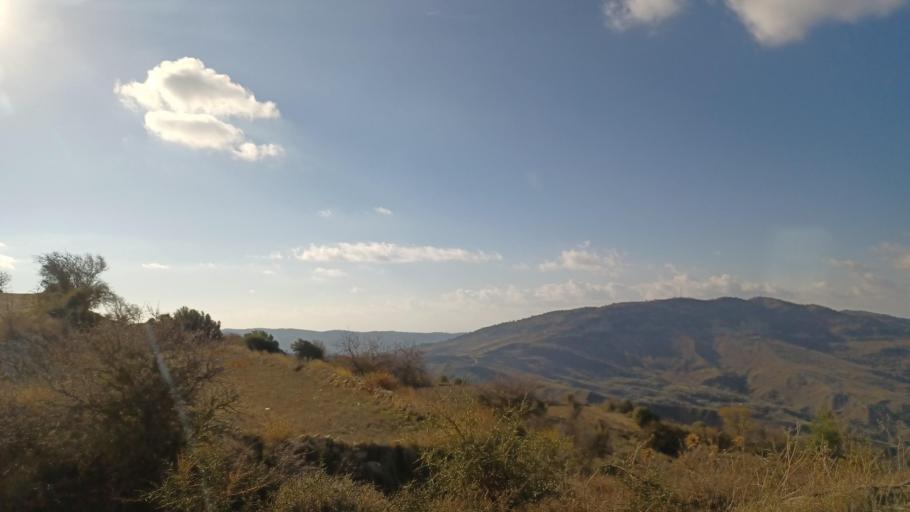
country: CY
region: Limassol
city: Pachna
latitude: 34.8377
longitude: 32.6828
